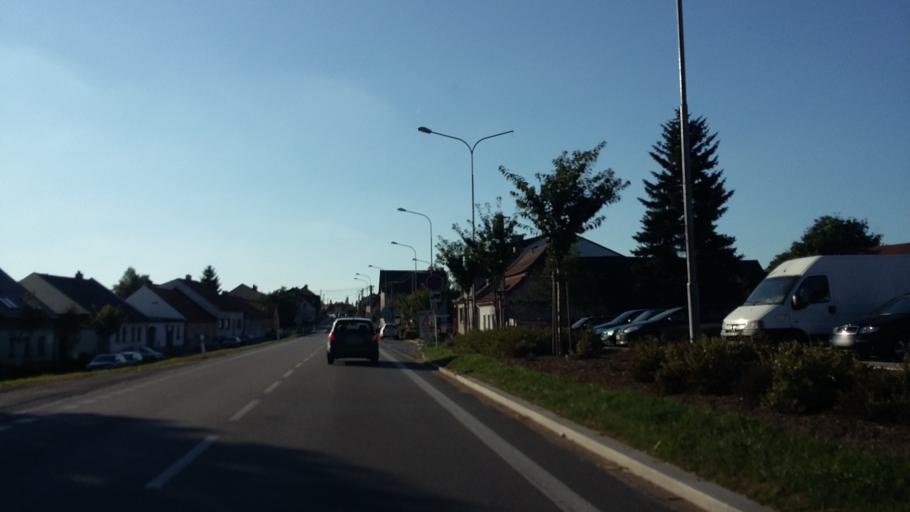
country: CZ
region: Vysocina
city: Merin
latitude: 49.3931
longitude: 15.8837
